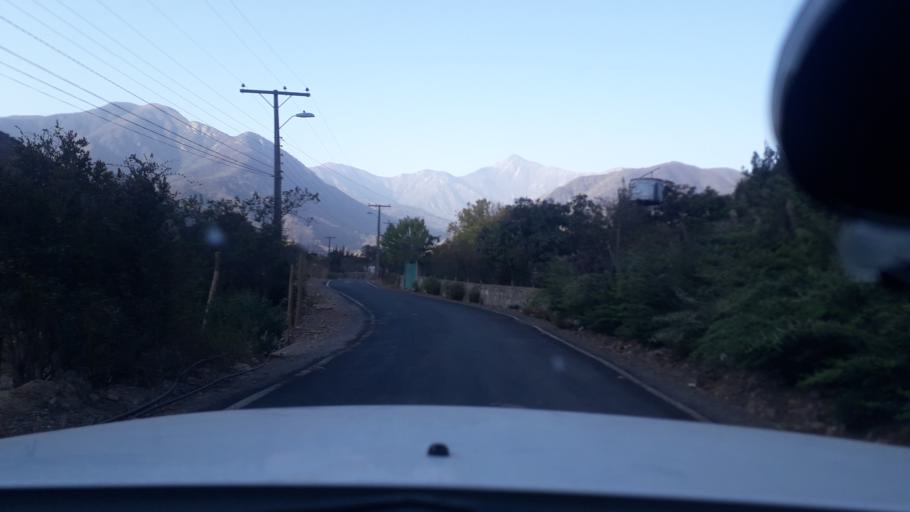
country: CL
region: Valparaiso
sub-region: Provincia de Marga Marga
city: Limache
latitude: -33.0605
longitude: -71.1162
